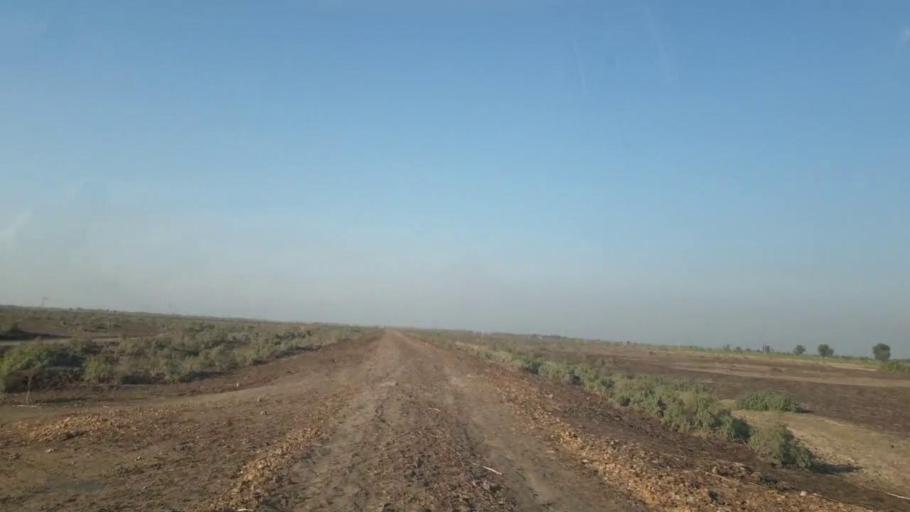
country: PK
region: Sindh
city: Mirpur Khas
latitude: 25.4382
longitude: 69.1012
